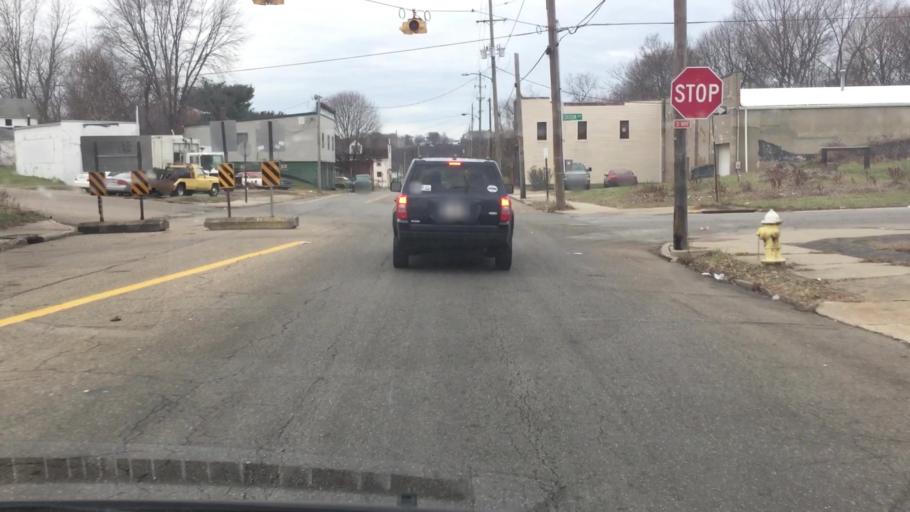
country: US
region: Ohio
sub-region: Summit County
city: Akron
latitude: 41.0544
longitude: -81.5319
